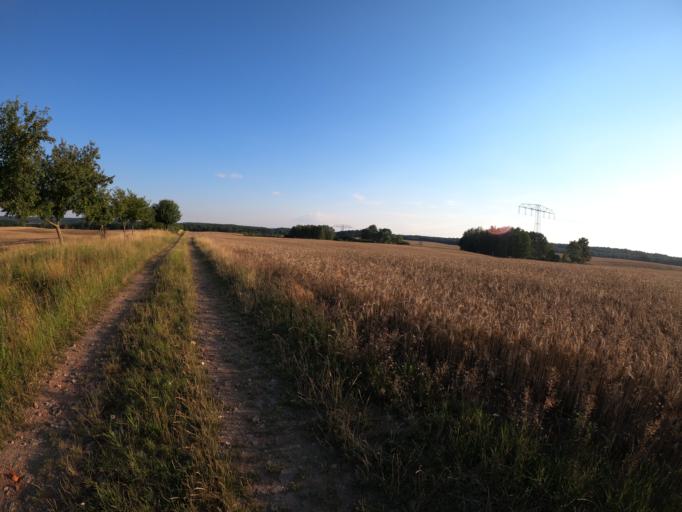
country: DE
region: Brandenburg
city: Althuttendorf
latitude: 53.0318
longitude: 13.8671
